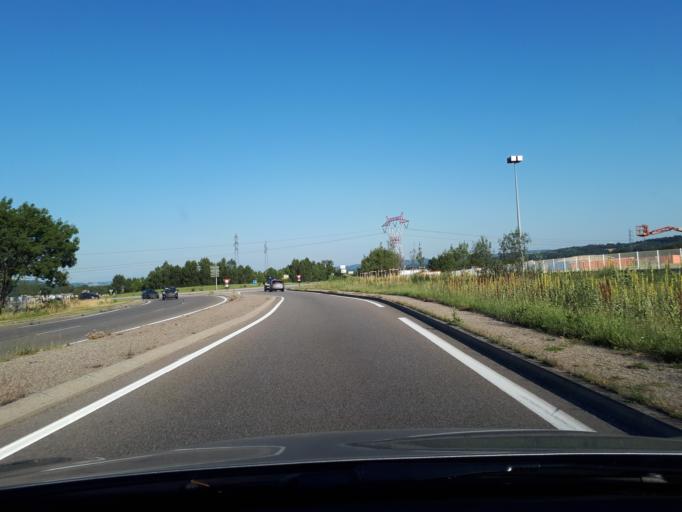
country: FR
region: Rhone-Alpes
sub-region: Departement de l'Isere
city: La Verpilliere
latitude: 45.6492
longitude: 5.1247
